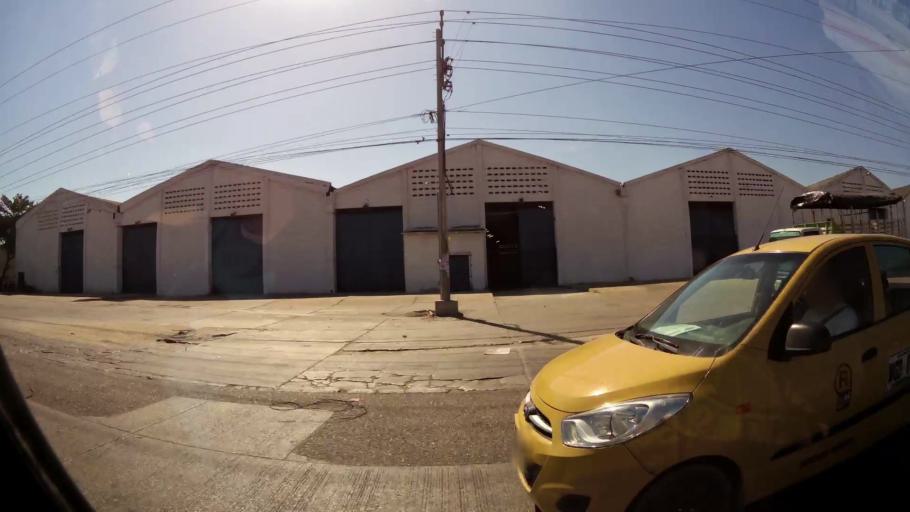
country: CO
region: Atlantico
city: Barranquilla
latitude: 10.9475
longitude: -74.7851
